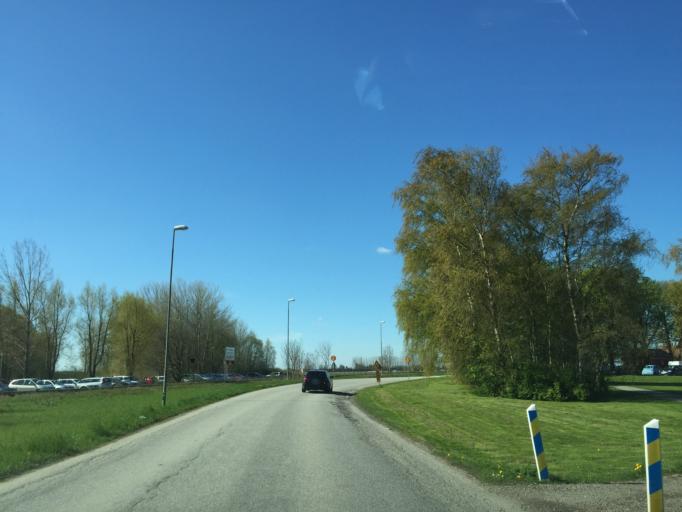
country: SE
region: Skane
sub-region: Staffanstorps Kommun
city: Staffanstorp
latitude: 55.6346
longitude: 13.2117
